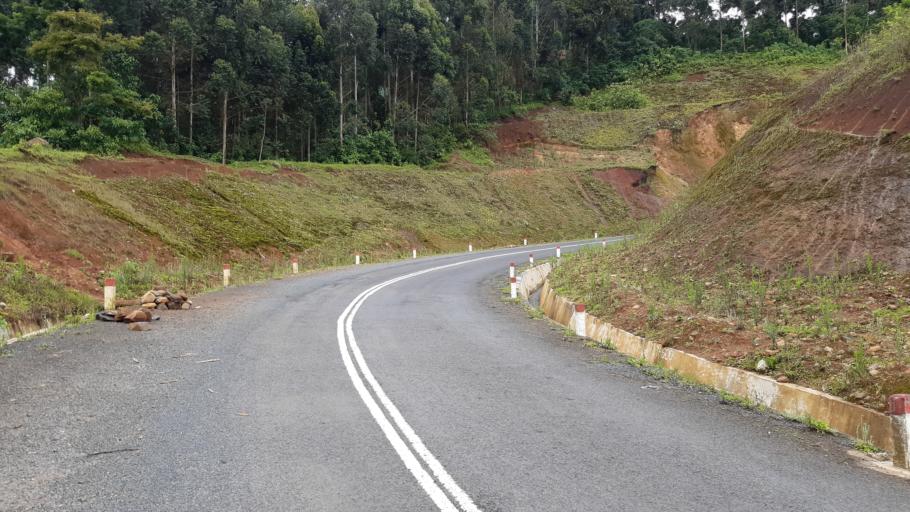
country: ET
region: Southern Nations, Nationalities, and People's Region
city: Bonga
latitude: 7.1754
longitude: 36.3154
